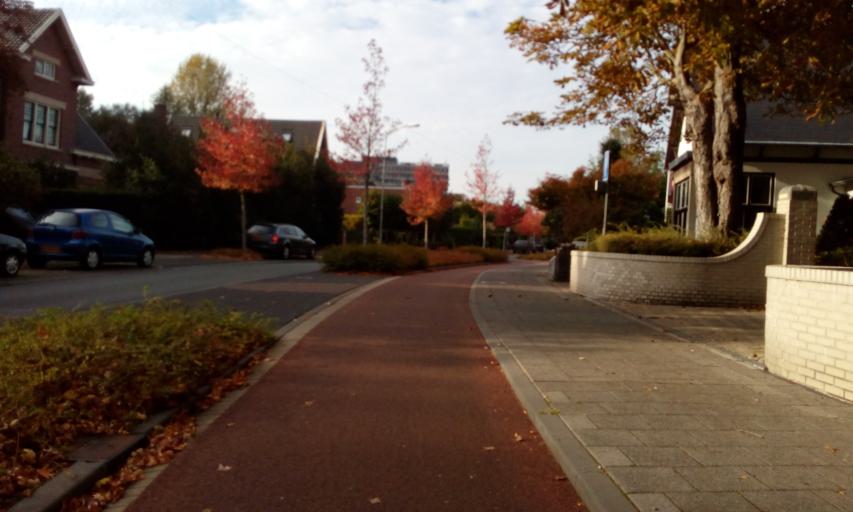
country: NL
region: South Holland
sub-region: Gemeente Leidschendam-Voorburg
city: Voorburg
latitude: 52.0820
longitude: 4.3911
